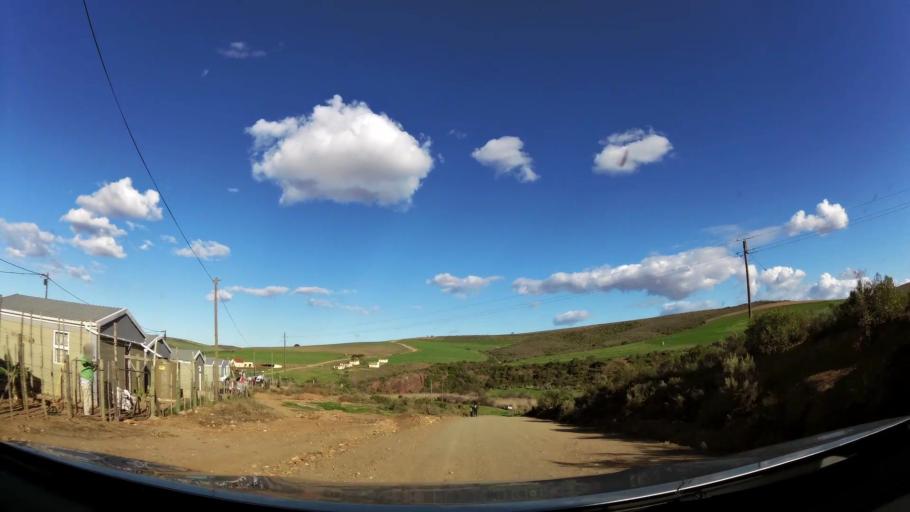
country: ZA
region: Western Cape
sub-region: Eden District Municipality
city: Riversdale
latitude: -34.1108
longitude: 20.9629
